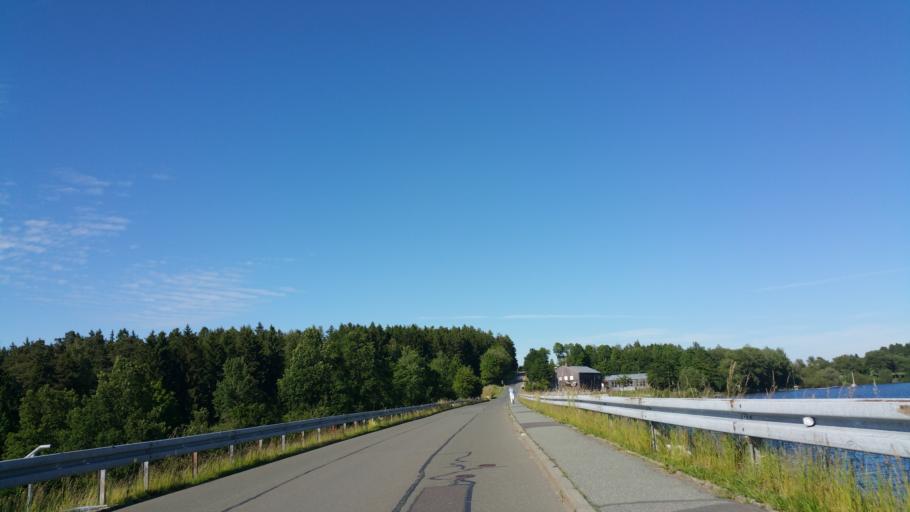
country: DE
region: Bavaria
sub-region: Upper Franconia
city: Schwarzenbach an der Saale
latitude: 50.2000
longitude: 11.9080
